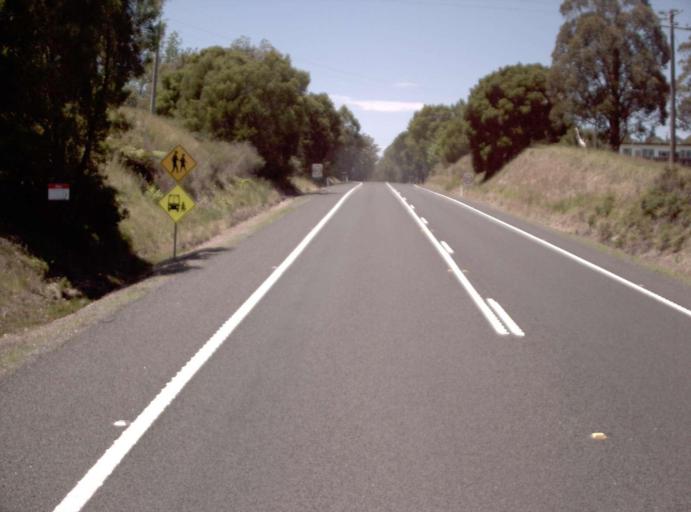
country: AU
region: Victoria
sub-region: East Gippsland
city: Lakes Entrance
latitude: -37.6998
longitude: 148.7180
